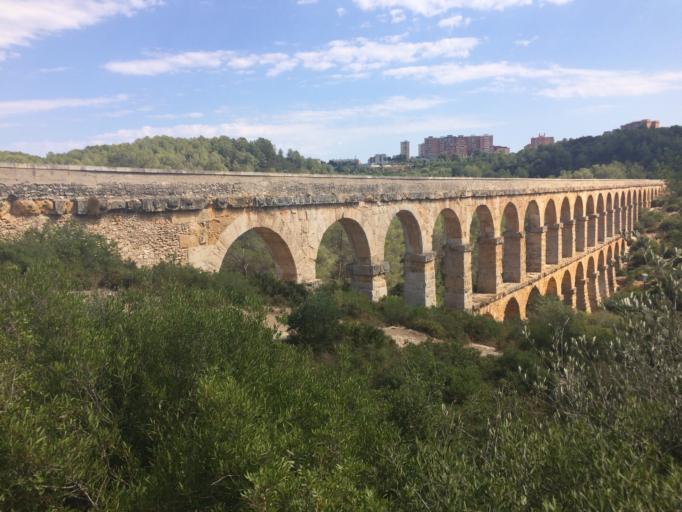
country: ES
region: Catalonia
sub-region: Provincia de Tarragona
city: els Pallaresos
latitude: 41.1468
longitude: 1.2433
